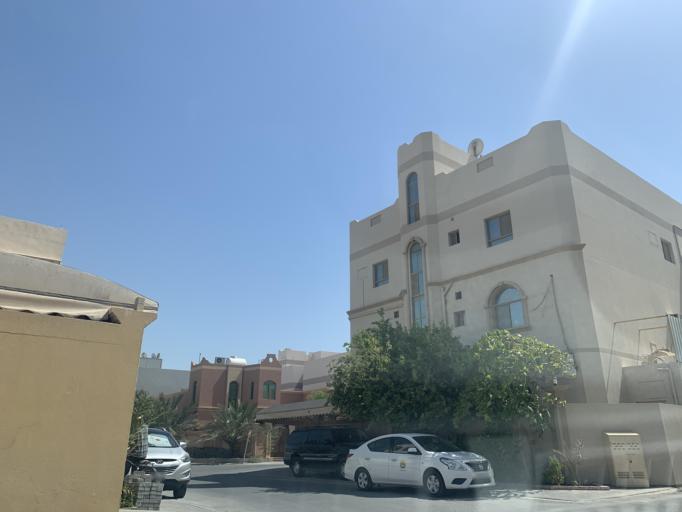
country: BH
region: Manama
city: Jidd Hafs
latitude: 26.2290
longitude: 50.5063
